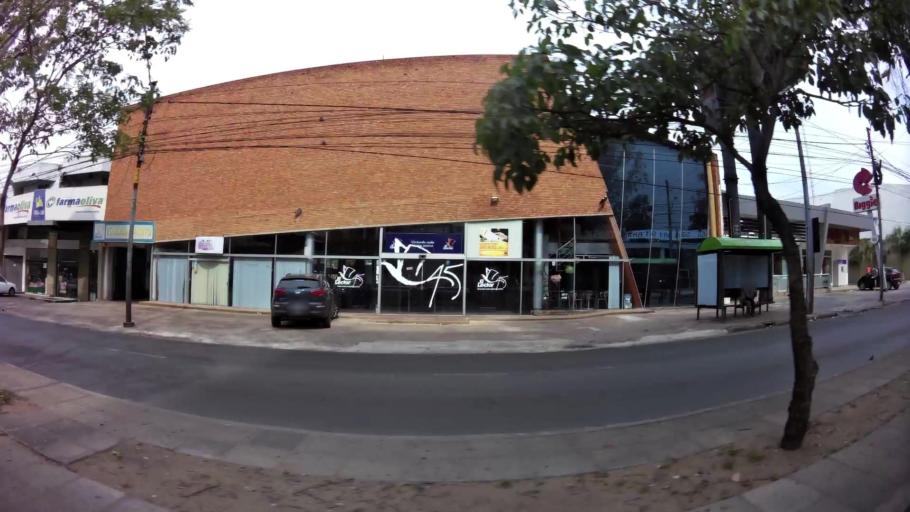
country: PY
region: Asuncion
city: Asuncion
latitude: -25.2873
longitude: -57.5723
